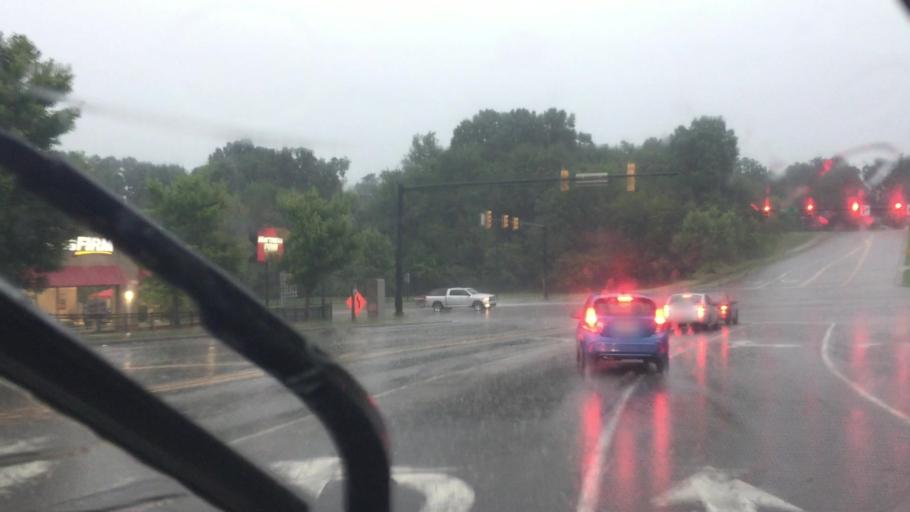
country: US
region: North Carolina
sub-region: Rowan County
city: Salisbury
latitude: 35.6544
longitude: -80.4579
